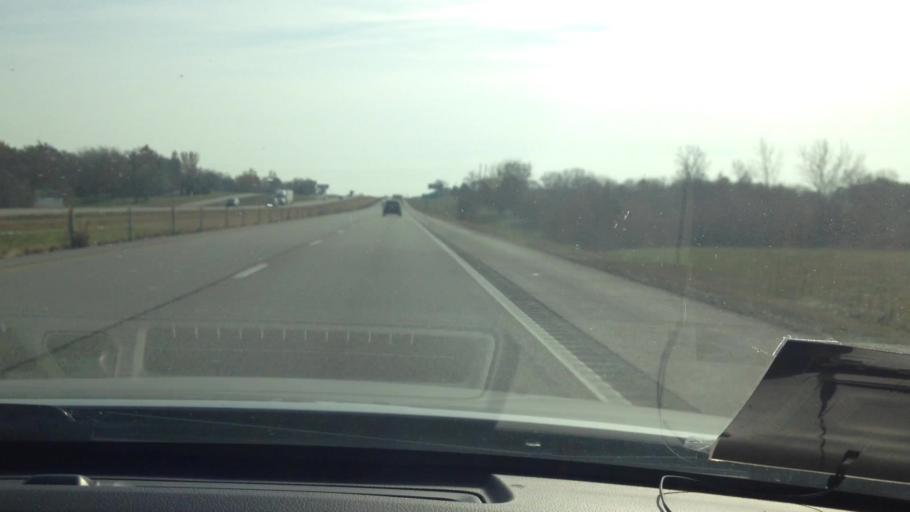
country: US
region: Missouri
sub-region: Cass County
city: Peculiar
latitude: 38.7164
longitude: -94.4491
